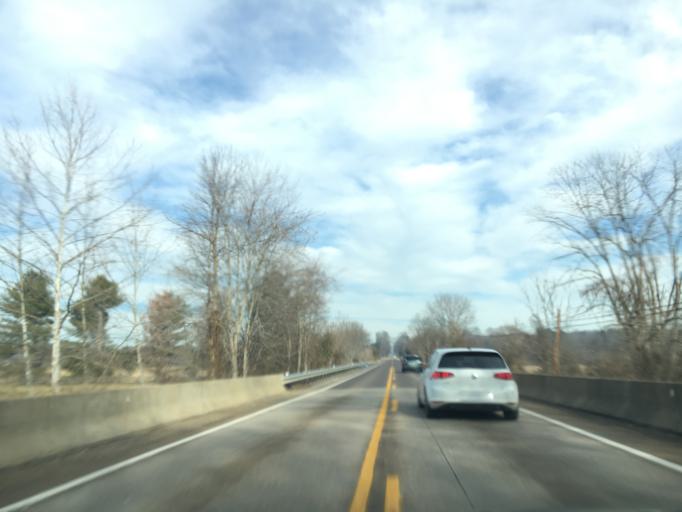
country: US
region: Virginia
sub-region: Culpeper County
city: Culpeper
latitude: 38.5899
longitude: -77.9682
